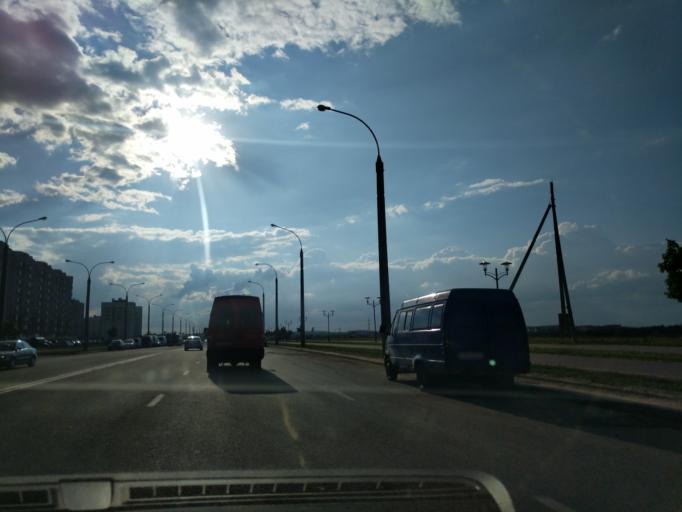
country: BY
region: Minsk
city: Zhdanovichy
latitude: 53.9166
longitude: 27.4260
